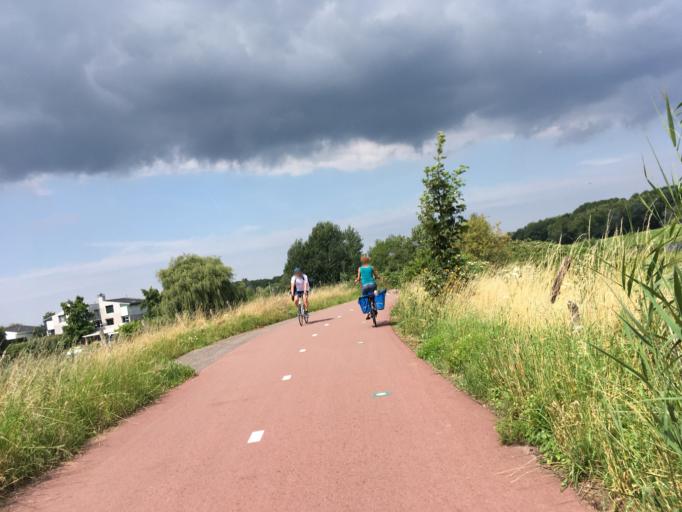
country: NL
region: North Holland
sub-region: Gemeente Zaanstad
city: Zaandam
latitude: 52.3872
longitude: 4.7603
